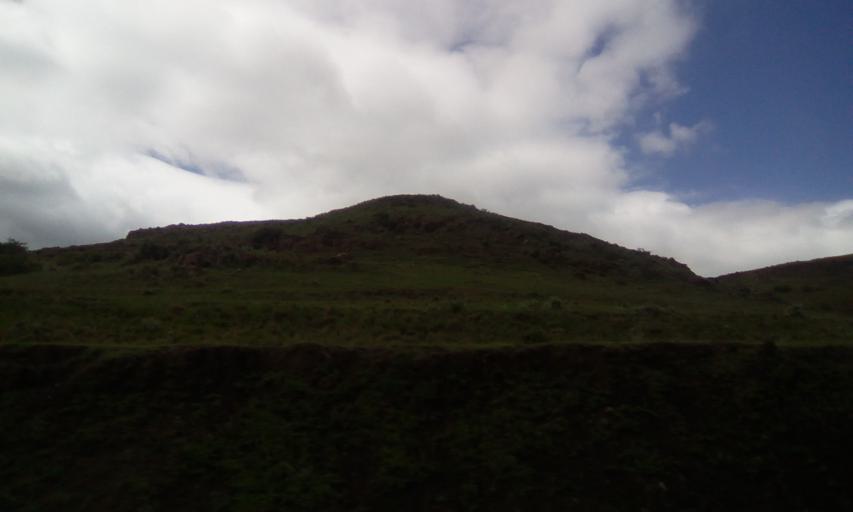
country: LS
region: Maseru
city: Nako
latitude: -29.6575
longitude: 27.8730
